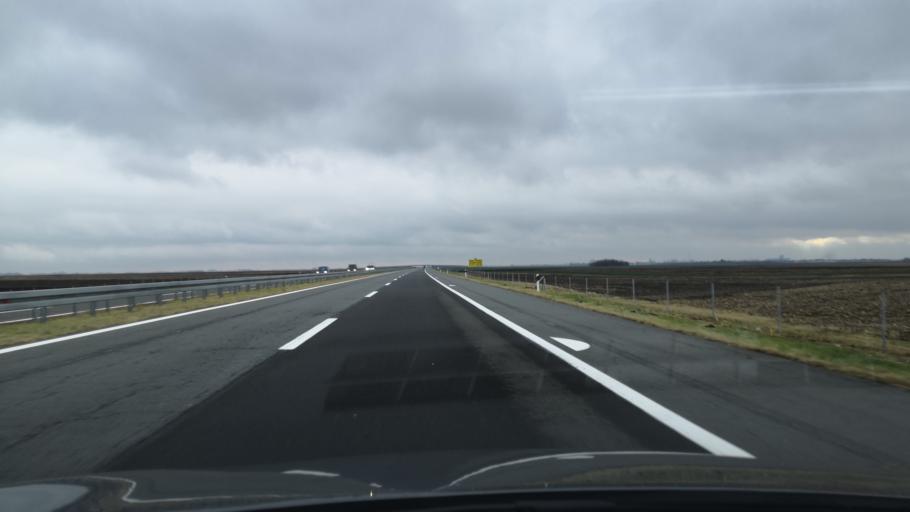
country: RS
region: Autonomna Pokrajina Vojvodina
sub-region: Severnobacki Okrug
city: Backa Topola
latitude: 45.8531
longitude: 19.6964
